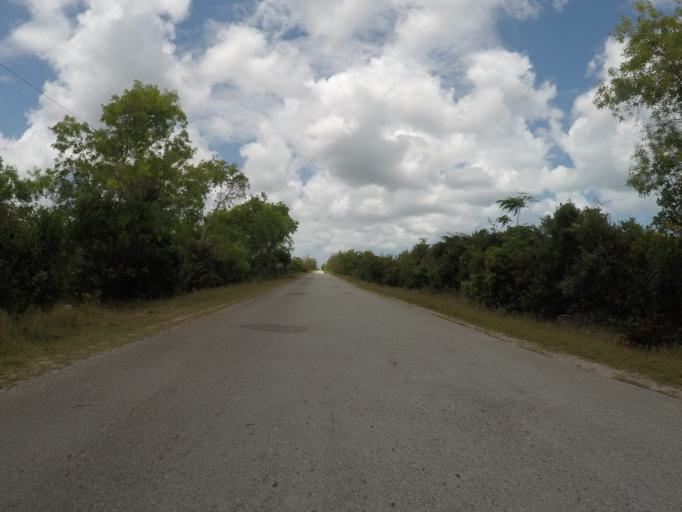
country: TZ
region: Zanzibar Central/South
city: Mahonda
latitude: -6.3222
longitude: 39.4350
